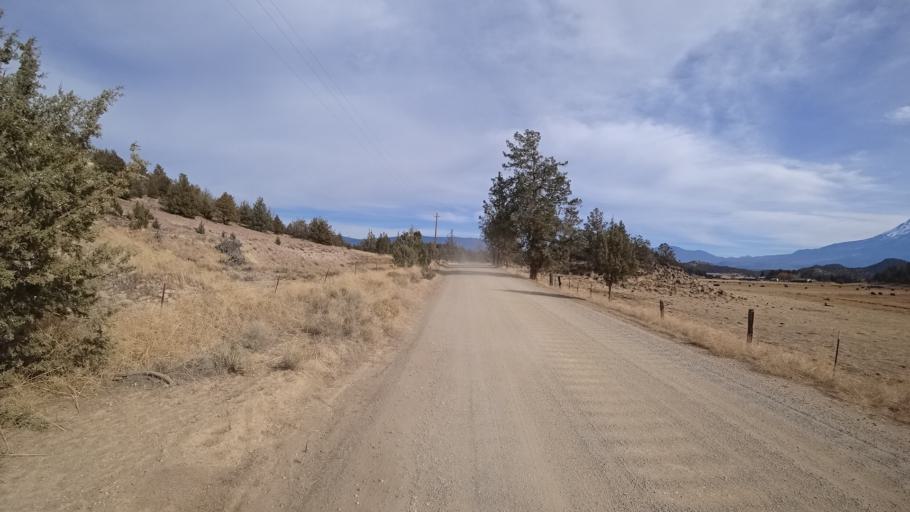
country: US
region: California
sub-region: Siskiyou County
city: Montague
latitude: 41.5855
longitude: -122.4458
